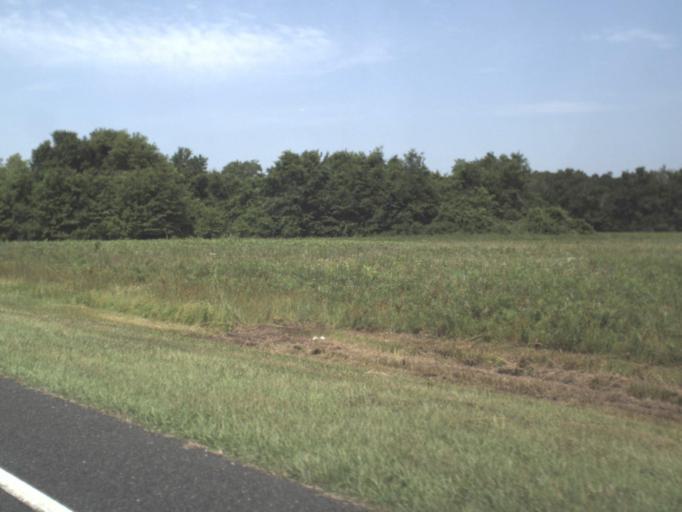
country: US
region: Florida
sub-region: Alachua County
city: Gainesville
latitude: 29.6891
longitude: -82.2866
